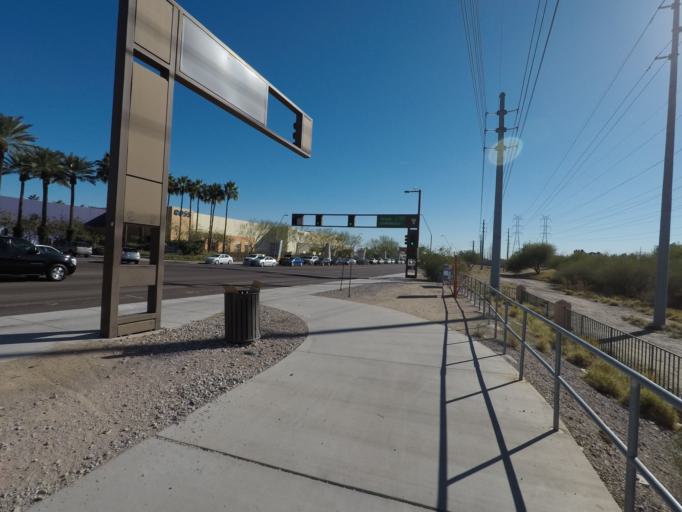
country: US
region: Arizona
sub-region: Maricopa County
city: Tempe
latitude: 33.4322
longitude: -111.9095
